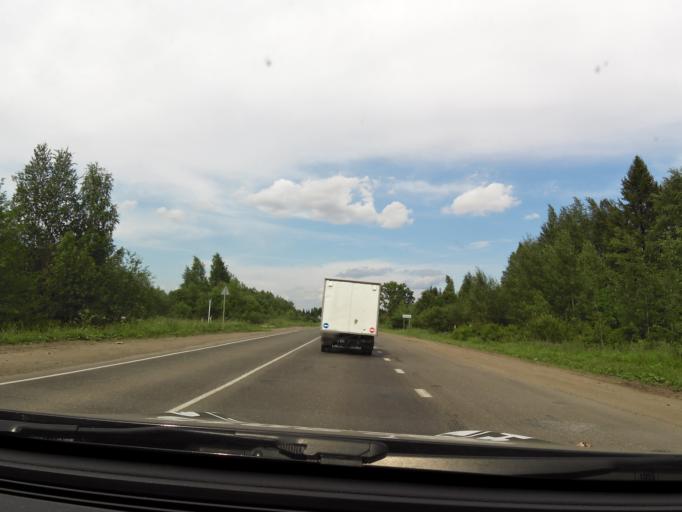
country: RU
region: Kirov
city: Stulovo
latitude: 58.7012
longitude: 50.0912
